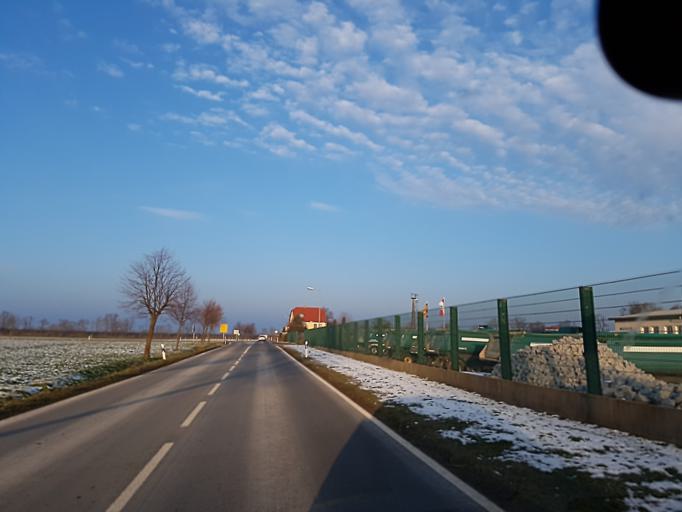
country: DE
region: Saxony
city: Oschatz
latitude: 51.2983
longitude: 13.1601
